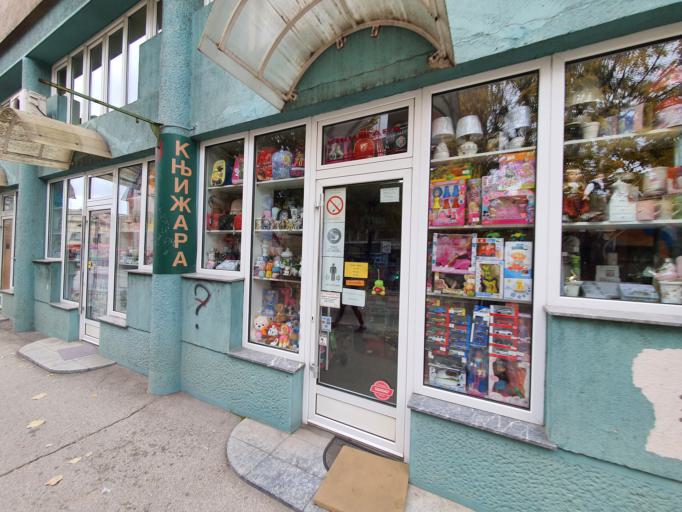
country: RS
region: Central Serbia
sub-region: Zlatiborski Okrug
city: Uzice
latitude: 43.8570
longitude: 19.8433
